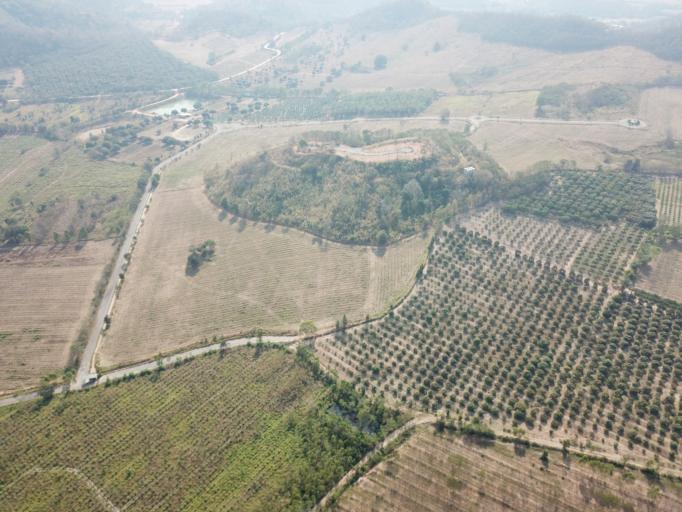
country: TH
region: Nakhon Ratchasima
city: Pak Chong
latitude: 14.7946
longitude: 101.3177
